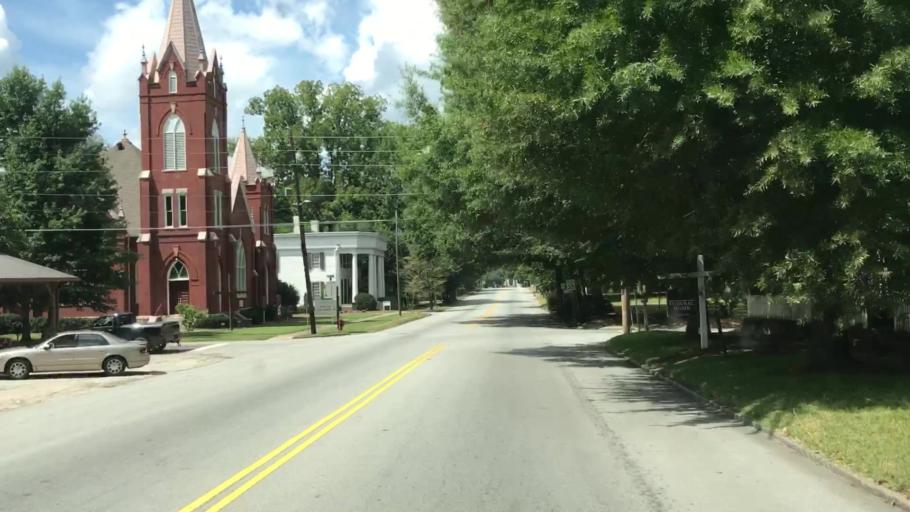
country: US
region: Georgia
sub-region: Greene County
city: Greensboro
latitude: 33.5761
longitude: -83.1837
